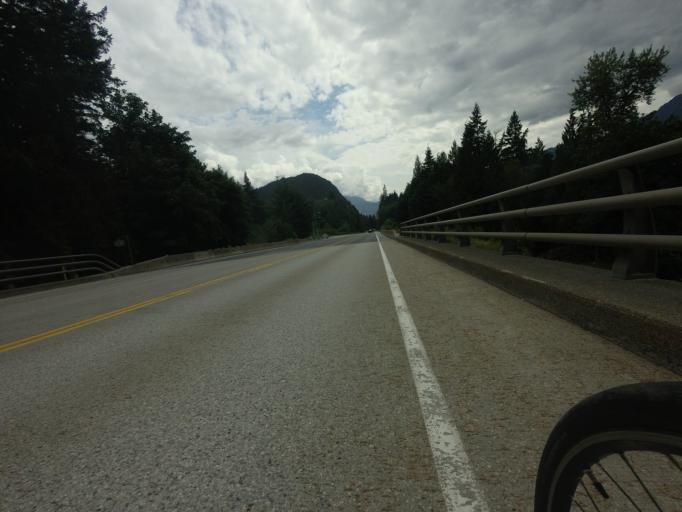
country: CA
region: British Columbia
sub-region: Greater Vancouver Regional District
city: Lions Bay
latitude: 49.7926
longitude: -123.1328
